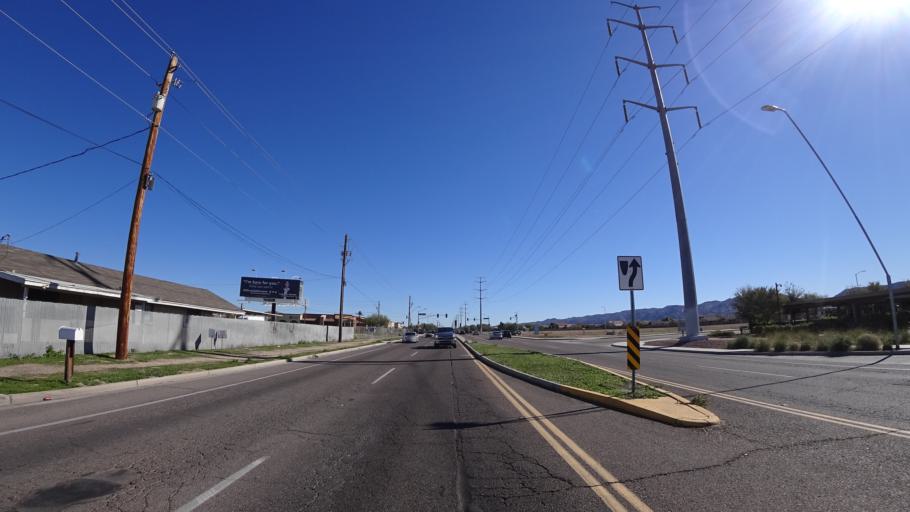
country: US
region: Arizona
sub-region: Maricopa County
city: Laveen
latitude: 33.3777
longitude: -112.1179
